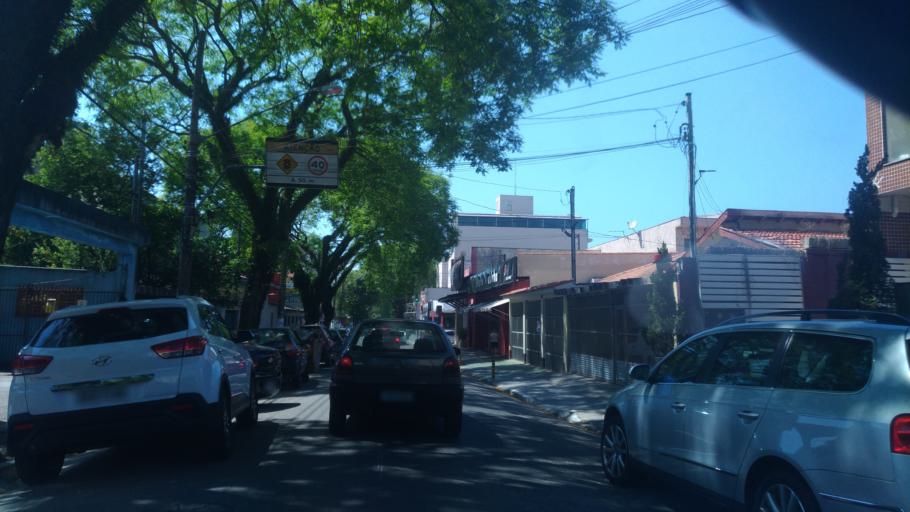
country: BR
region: Sao Paulo
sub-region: Sao Bernardo Do Campo
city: Sao Bernardo do Campo
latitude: -23.6676
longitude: -46.5887
